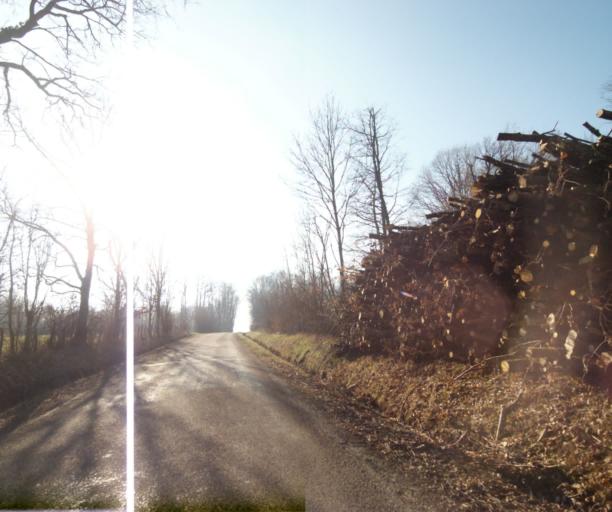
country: FR
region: Champagne-Ardenne
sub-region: Departement de la Haute-Marne
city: Wassy
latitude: 48.5092
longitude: 4.9641
